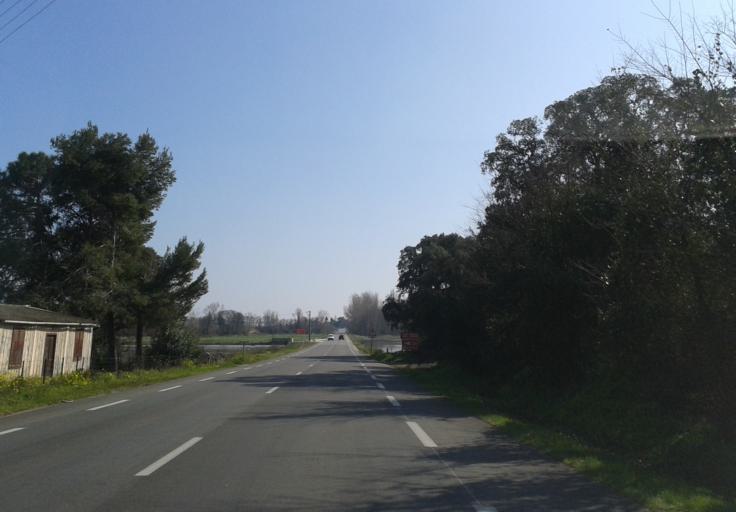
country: FR
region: Corsica
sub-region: Departement de la Haute-Corse
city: Cervione
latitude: 42.2937
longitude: 9.5470
